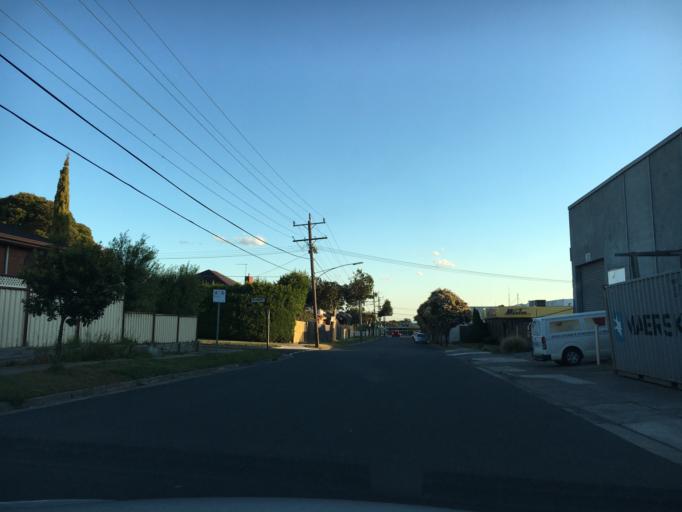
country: AU
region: Victoria
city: Clayton
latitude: -37.9106
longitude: 145.1130
